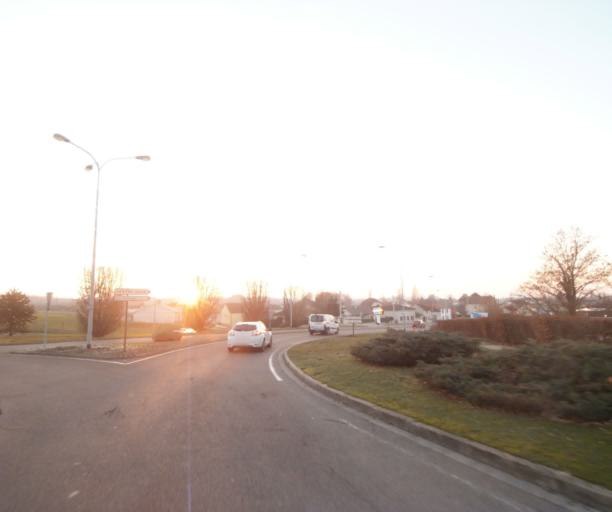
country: FR
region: Champagne-Ardenne
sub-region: Departement de la Haute-Marne
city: Saint-Dizier
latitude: 48.6266
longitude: 4.9631
